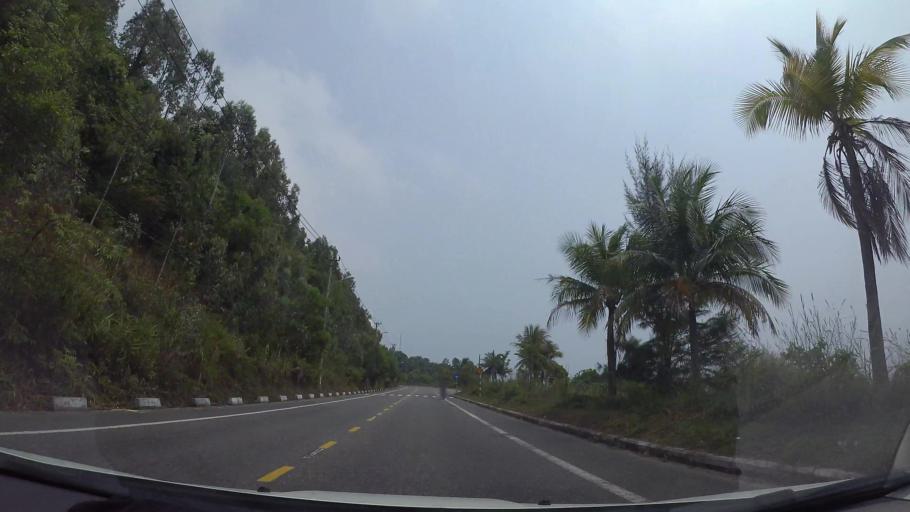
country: VN
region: Da Nang
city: Son Tra
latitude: 16.1002
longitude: 108.2724
